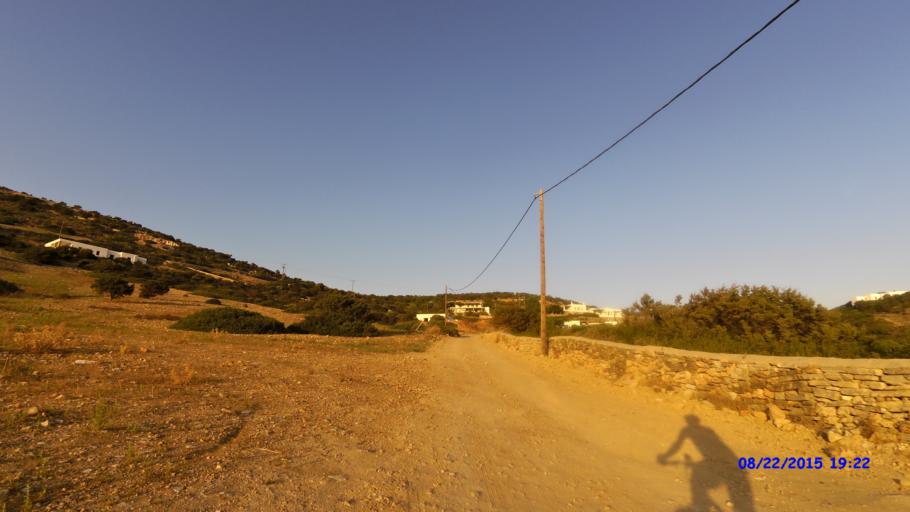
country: GR
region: South Aegean
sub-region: Nomos Kykladon
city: Antiparos
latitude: 36.9727
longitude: 25.0427
